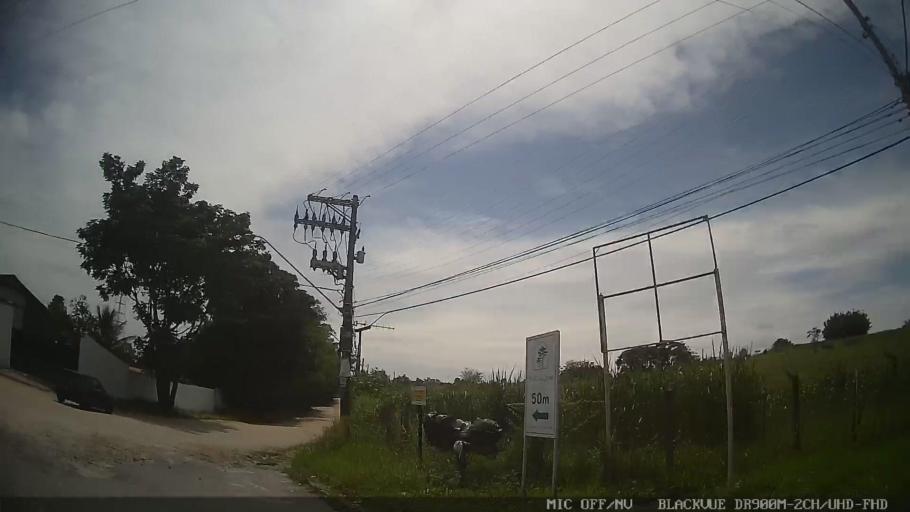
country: BR
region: Sao Paulo
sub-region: Santa Isabel
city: Santa Isabel
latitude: -23.3630
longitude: -46.1772
